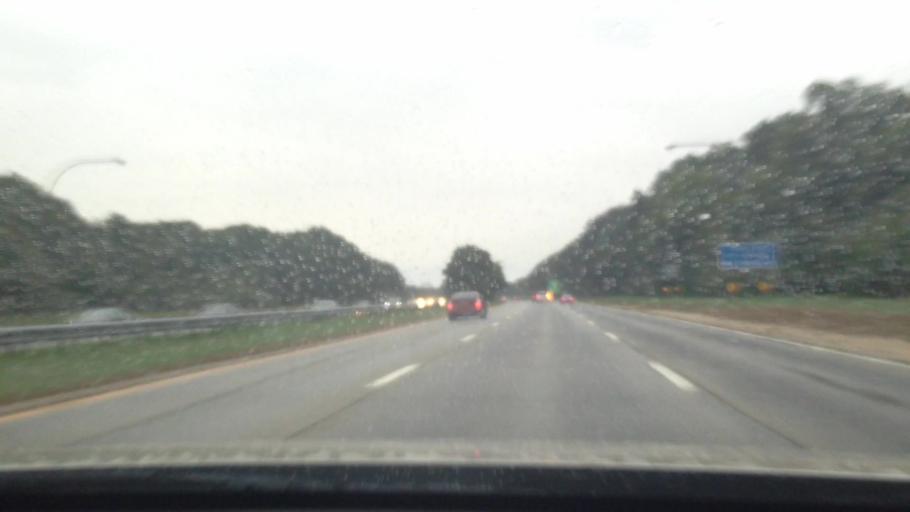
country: US
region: New York
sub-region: Suffolk County
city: Islip
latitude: 40.7547
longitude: -73.2261
